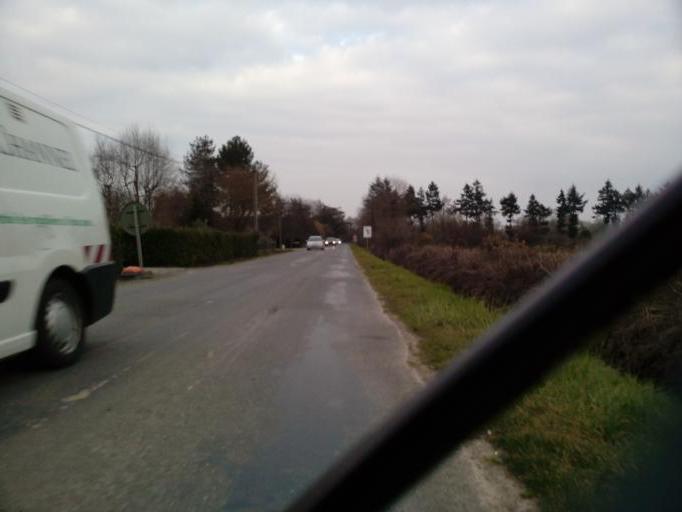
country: FR
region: Brittany
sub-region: Departement d'Ille-et-Vilaine
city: Talensac
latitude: 48.1054
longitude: -1.9164
